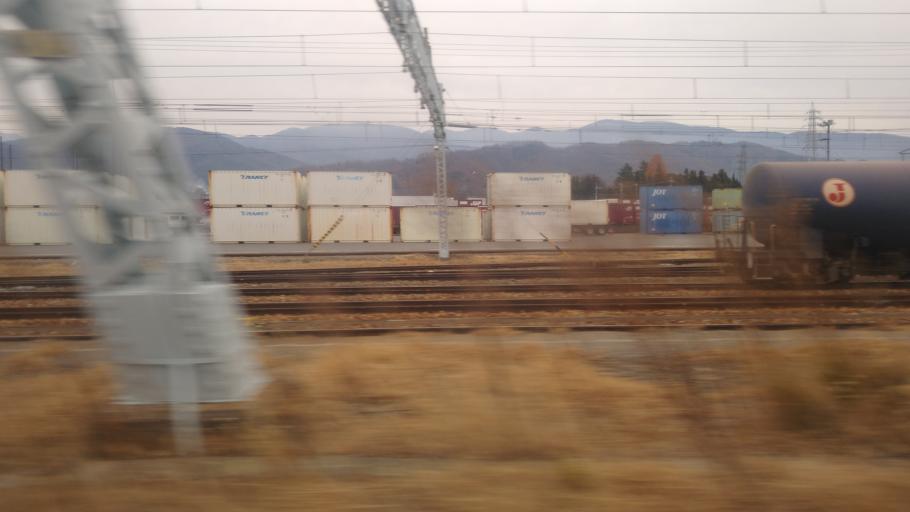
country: JP
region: Nagano
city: Matsumoto
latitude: 36.2115
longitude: 137.9699
